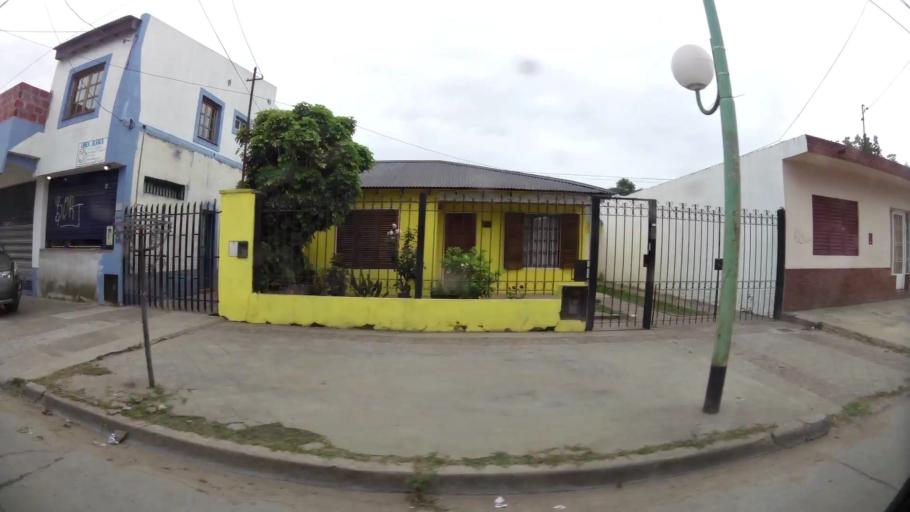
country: AR
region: Buenos Aires
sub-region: Partido de Zarate
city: Zarate
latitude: -34.1103
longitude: -59.0261
